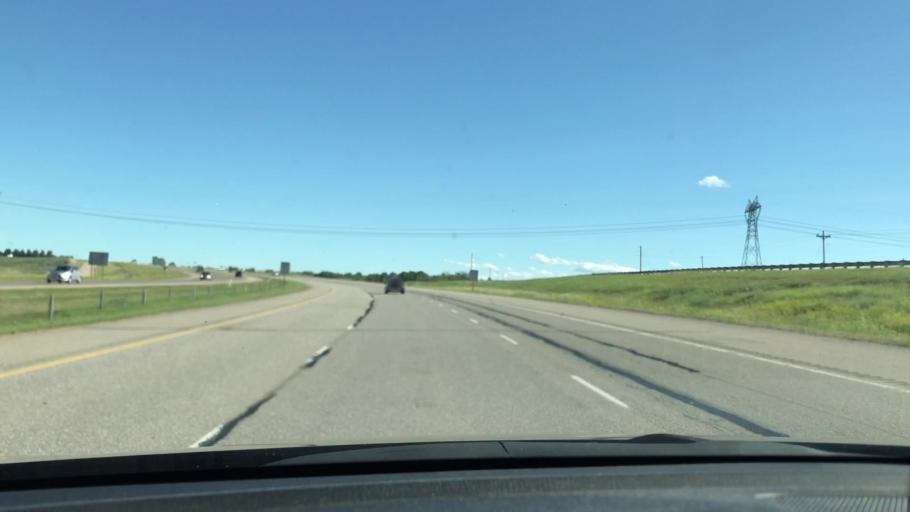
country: CA
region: Alberta
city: Crossfield
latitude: 51.4642
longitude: -114.0252
